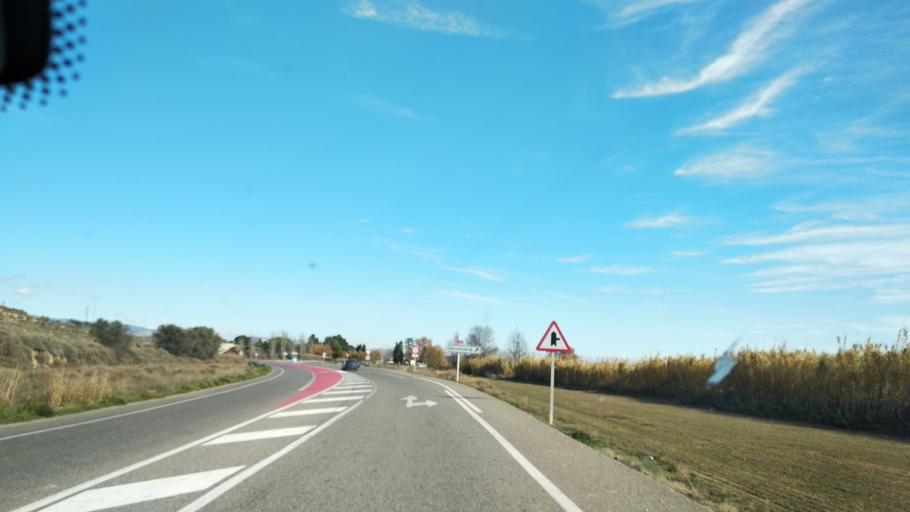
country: ES
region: Catalonia
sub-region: Provincia de Lleida
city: Vallfogona de Balaguer
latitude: 41.7664
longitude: 0.7848
